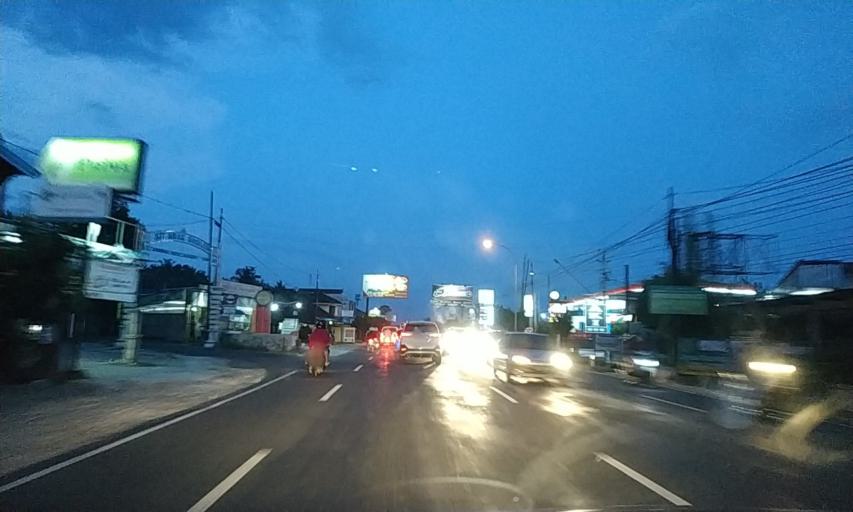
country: ID
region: Daerah Istimewa Yogyakarta
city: Godean
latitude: -7.8128
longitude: 110.2663
